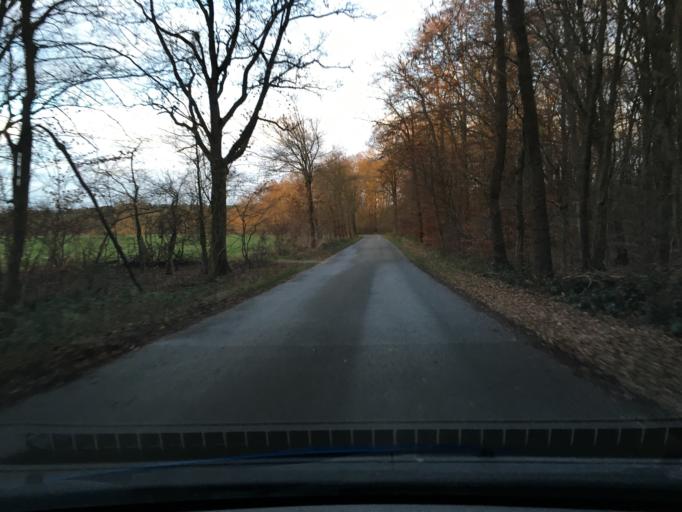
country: DE
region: Lower Saxony
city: Amelinghausen
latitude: 53.1380
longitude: 10.2038
